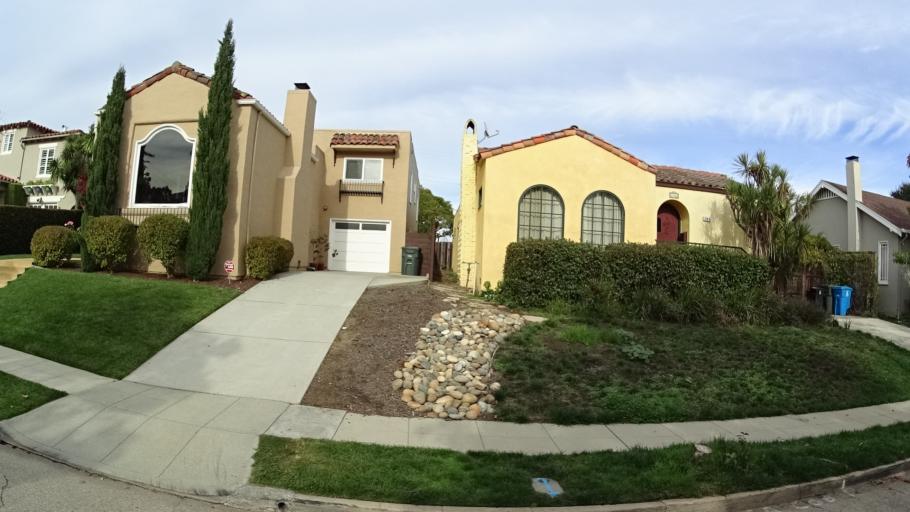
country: US
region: California
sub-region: San Mateo County
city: Hillsborough
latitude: 37.5821
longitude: -122.3753
